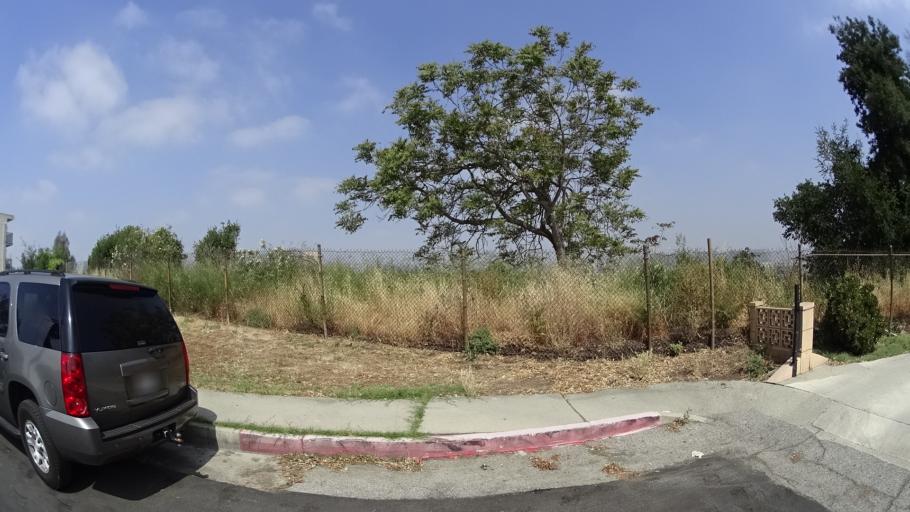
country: US
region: California
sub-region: Los Angeles County
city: Los Angeles
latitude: 34.0541
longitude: -118.2206
